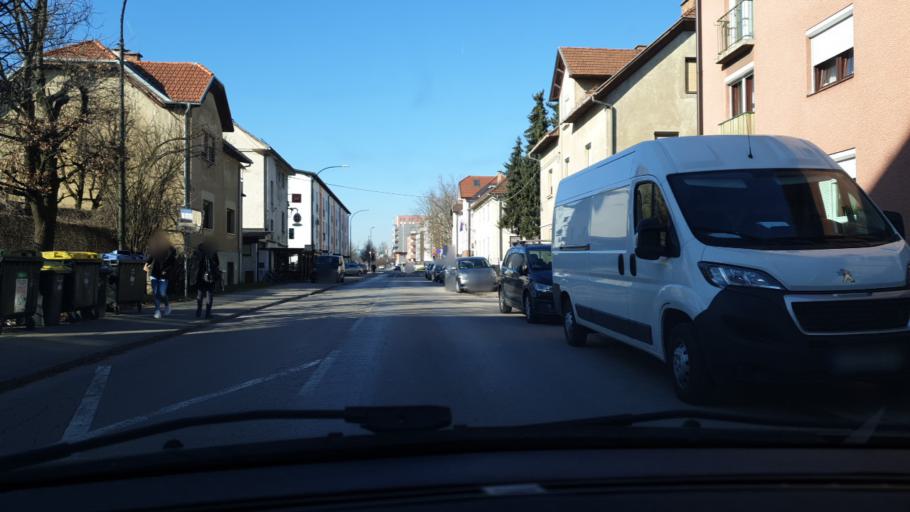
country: SI
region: Ljubljana
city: Ljubljana
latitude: 46.0621
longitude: 14.5323
